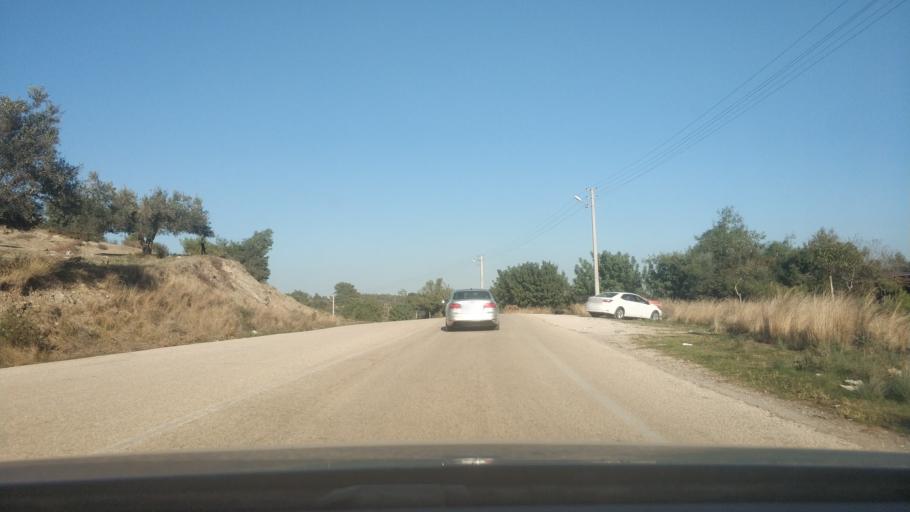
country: TR
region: Adana
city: Adana
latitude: 37.1015
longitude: 35.2909
